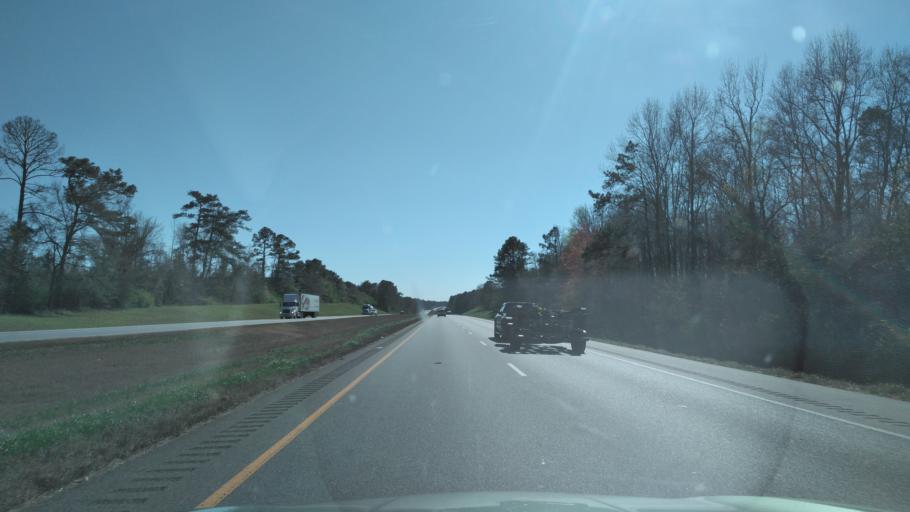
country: US
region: Alabama
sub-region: Lowndes County
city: Fort Deposit
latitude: 31.9349
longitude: -86.5682
